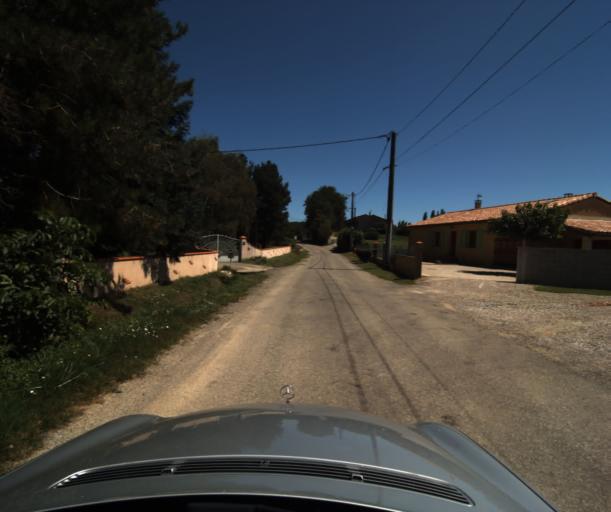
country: FR
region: Midi-Pyrenees
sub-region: Departement de l'Ariege
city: Belesta
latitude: 42.9861
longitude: 1.9146
